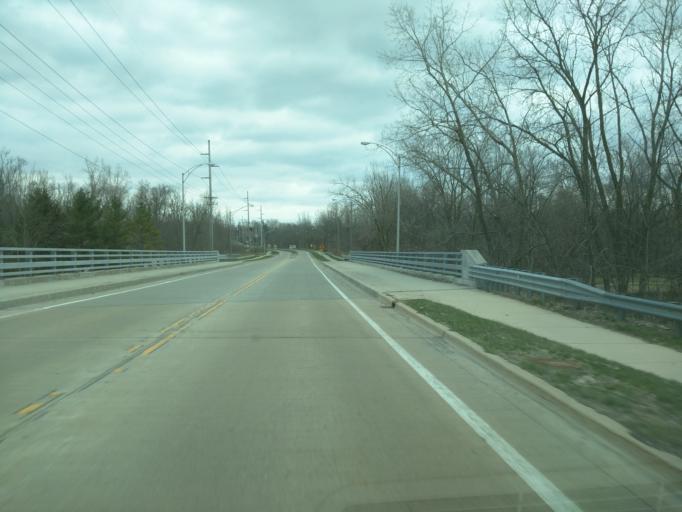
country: US
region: Michigan
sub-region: Ingham County
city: Lansing
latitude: 42.7169
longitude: -84.5225
